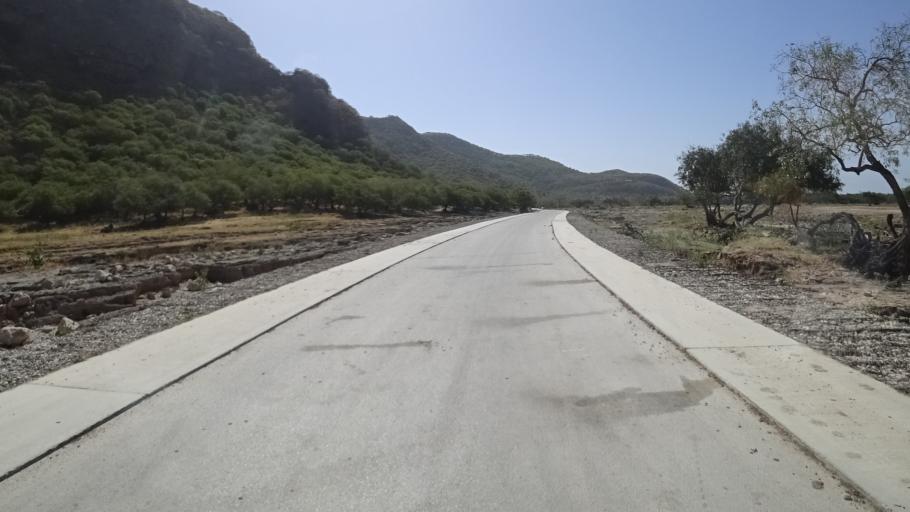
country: OM
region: Zufar
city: Salalah
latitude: 17.0862
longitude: 54.4351
